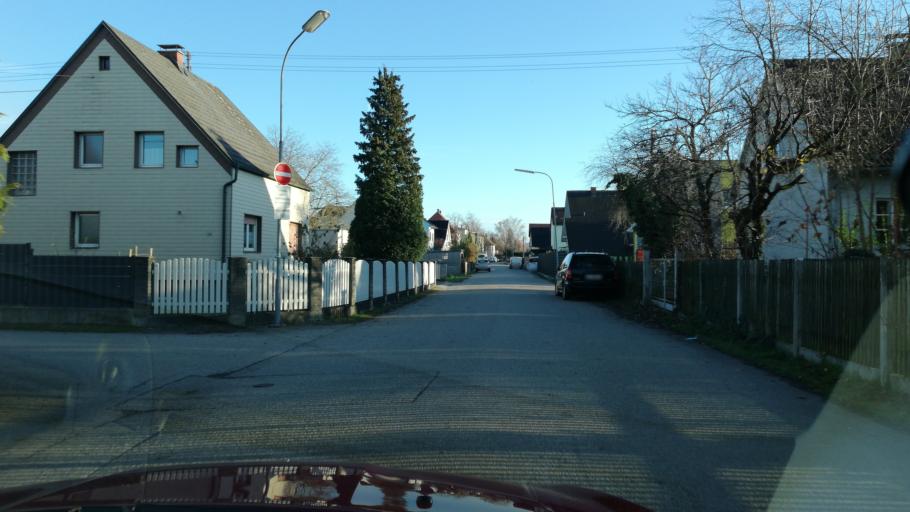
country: AT
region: Upper Austria
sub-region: Politischer Bezirk Linz-Land
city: Traun
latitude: 48.2306
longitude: 14.2486
